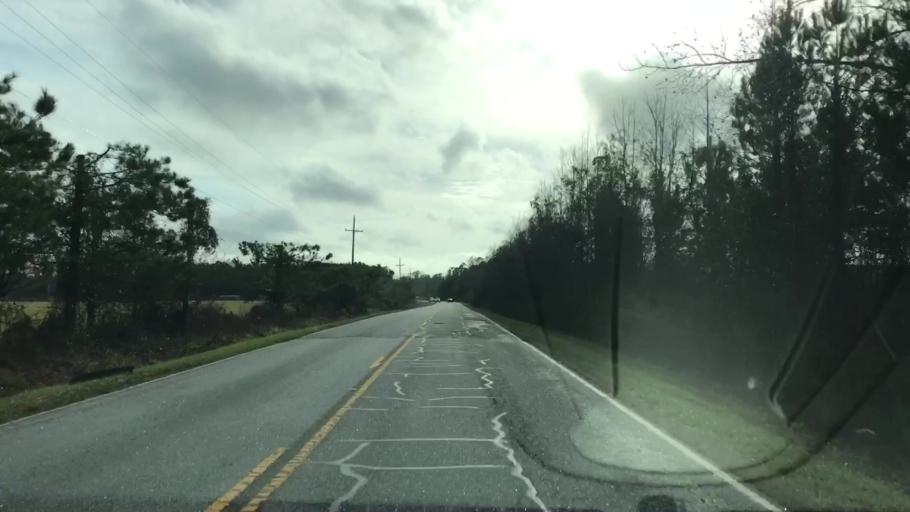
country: US
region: South Carolina
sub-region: Williamsburg County
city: Andrews
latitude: 33.3528
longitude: -79.6594
